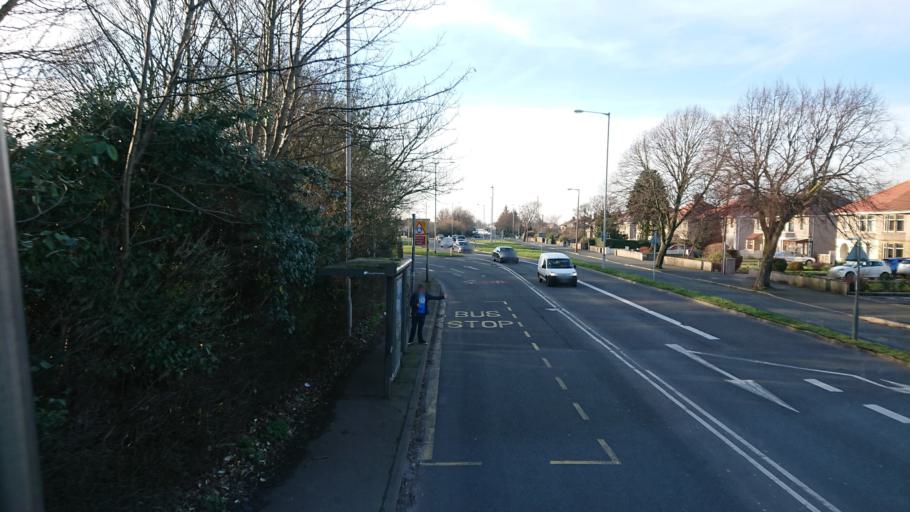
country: GB
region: England
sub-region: Lancashire
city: Lancaster
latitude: 54.0590
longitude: -2.8236
